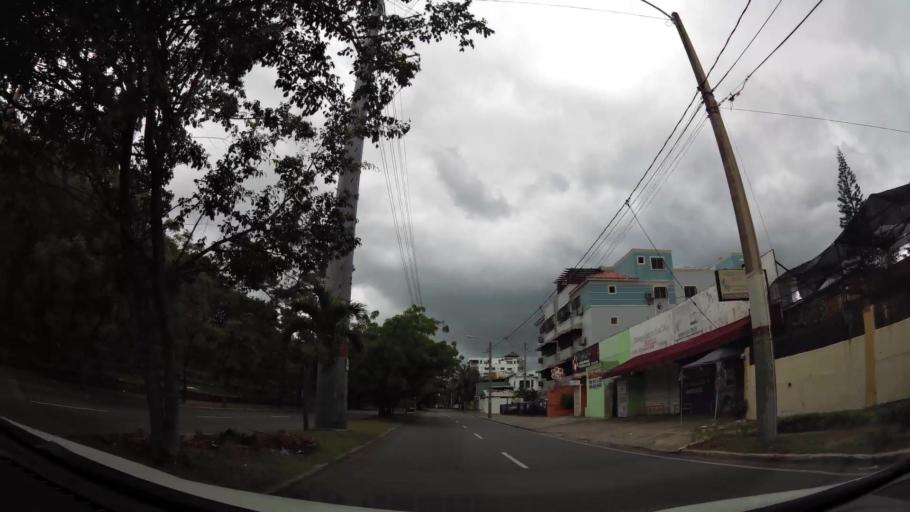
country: DO
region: Nacional
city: Bella Vista
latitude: 18.4486
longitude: -69.9386
